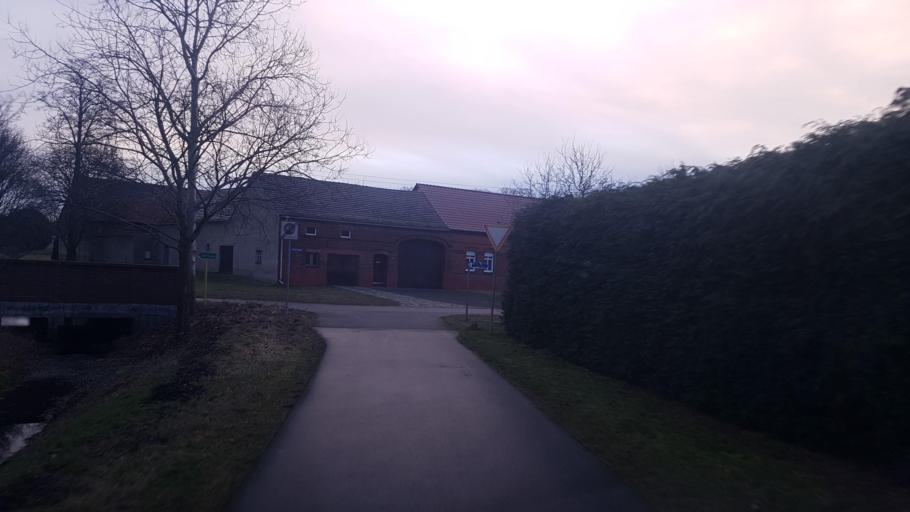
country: DE
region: Brandenburg
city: Dahme
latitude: 51.8679
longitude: 13.4593
